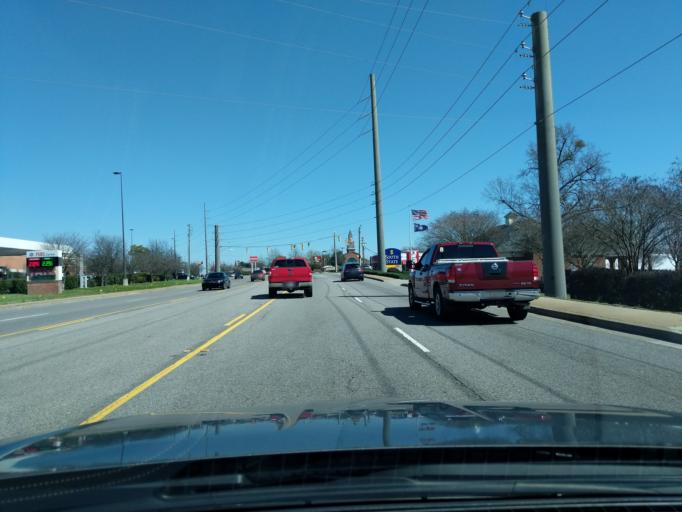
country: US
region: South Carolina
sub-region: Aiken County
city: Aiken
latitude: 33.5224
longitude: -81.7232
